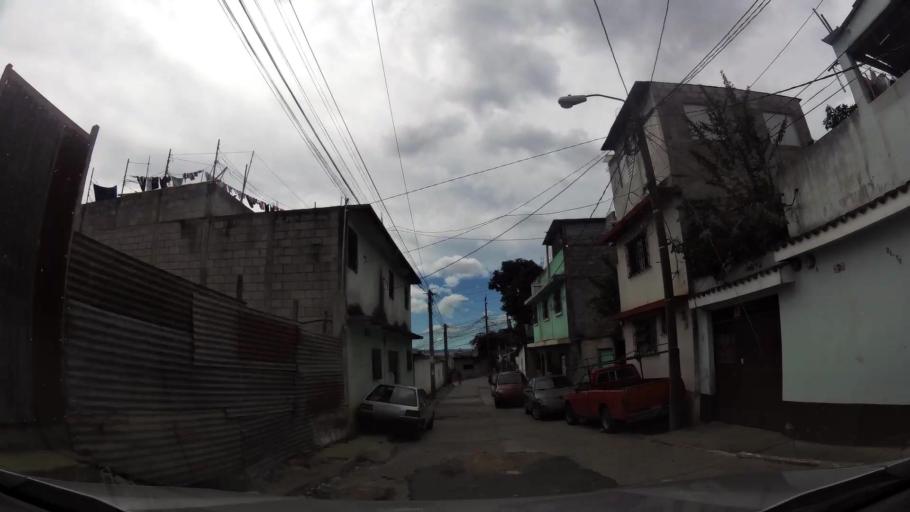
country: GT
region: Guatemala
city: Santa Catarina Pinula
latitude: 14.5690
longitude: -90.5333
